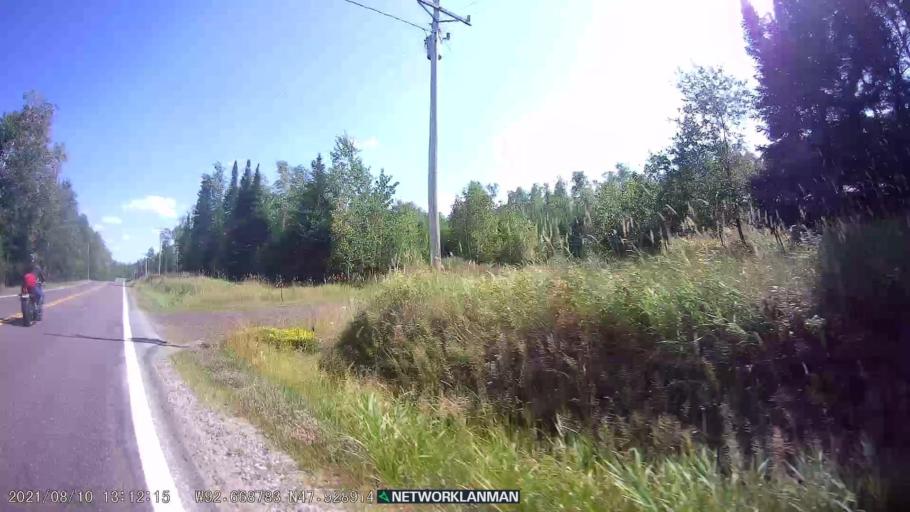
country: US
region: Minnesota
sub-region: Saint Louis County
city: Mountain Iron
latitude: 47.9288
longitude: -92.6685
